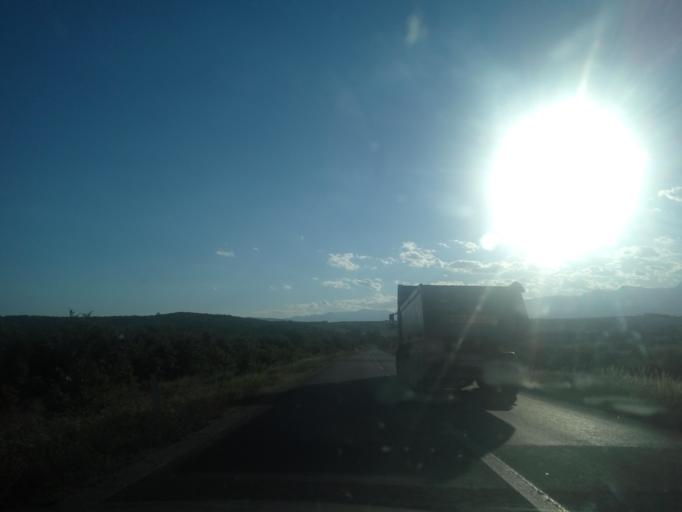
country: XK
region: Gjakova
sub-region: Komuna e Gjakoves
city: Gjakove
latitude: 42.4355
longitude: 20.4714
